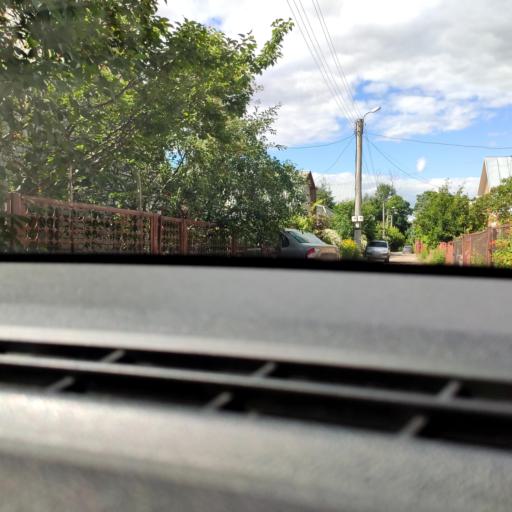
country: RU
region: Samara
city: Podstepki
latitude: 53.5839
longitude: 49.0690
